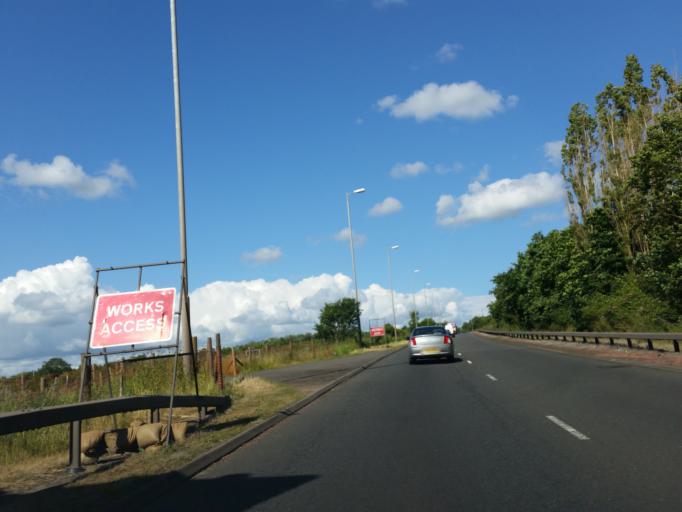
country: GB
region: Scotland
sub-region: South Lanarkshire
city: Bothwell
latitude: 55.8075
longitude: -4.0453
